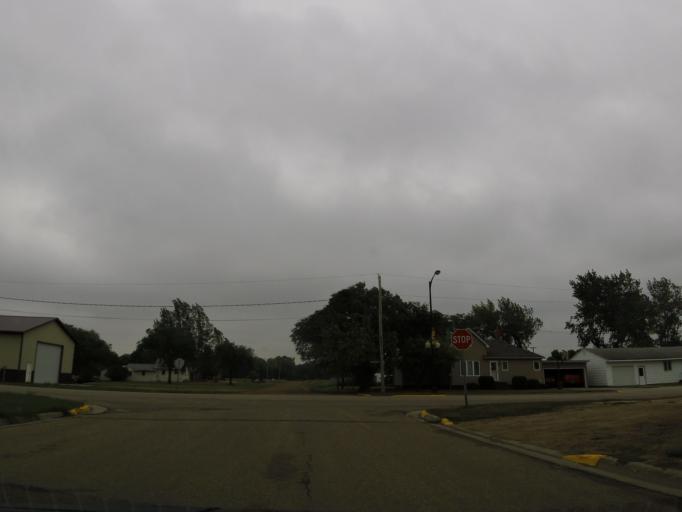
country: US
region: Minnesota
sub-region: Marshall County
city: Warren
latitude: 48.3360
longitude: -96.8167
